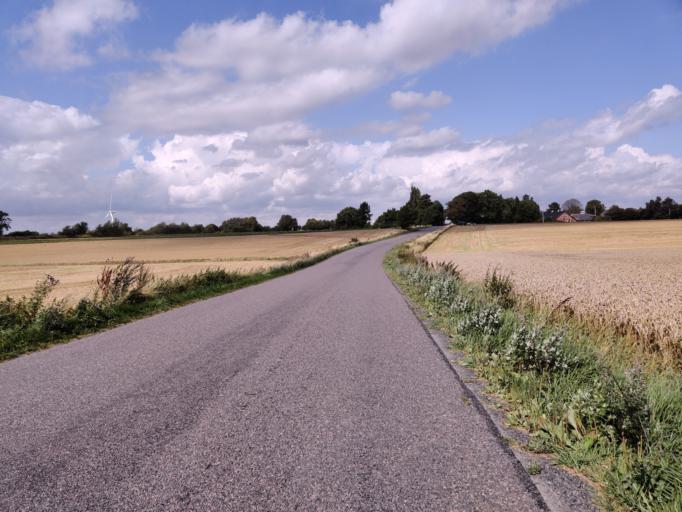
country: DK
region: Zealand
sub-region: Guldborgsund Kommune
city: Nykobing Falster
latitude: 54.6746
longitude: 11.9005
